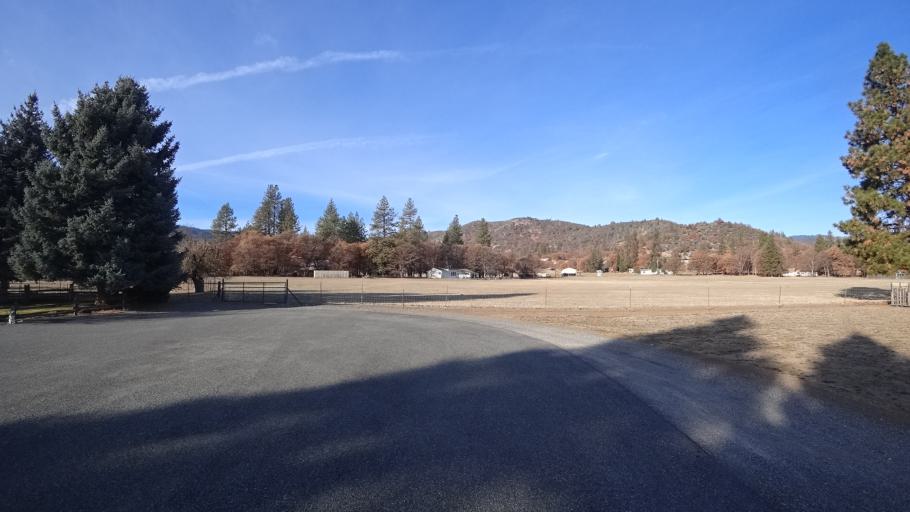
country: US
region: California
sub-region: Siskiyou County
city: Yreka
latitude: 41.6800
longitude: -122.6386
